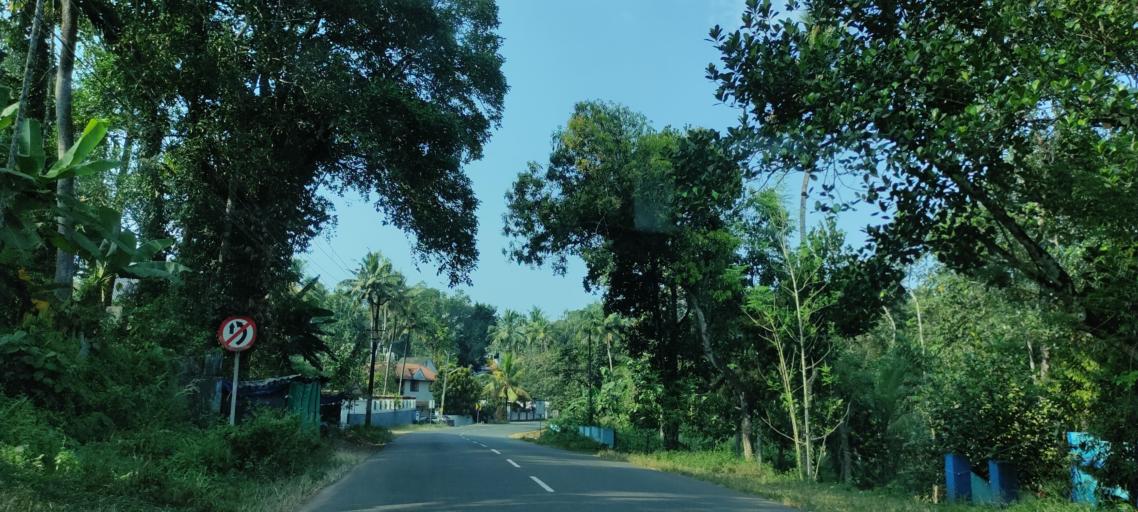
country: IN
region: Kerala
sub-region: Pattanamtitta
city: Adur
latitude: 9.1051
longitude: 76.6905
